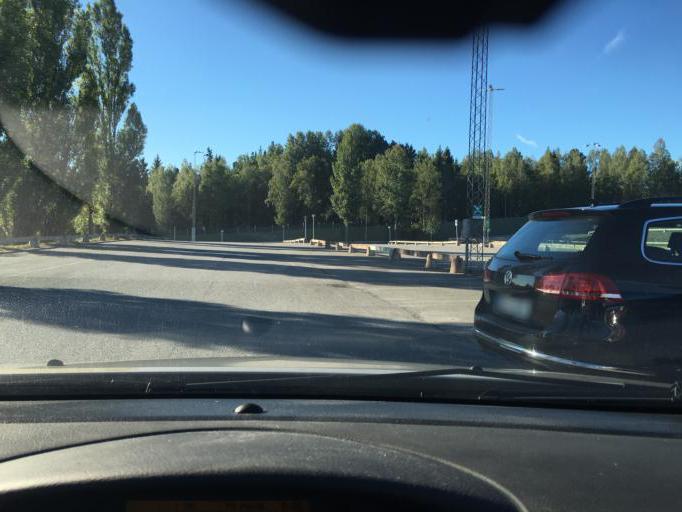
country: SE
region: Stockholm
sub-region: Sodertalje Kommun
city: Pershagen
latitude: 59.1660
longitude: 17.6352
